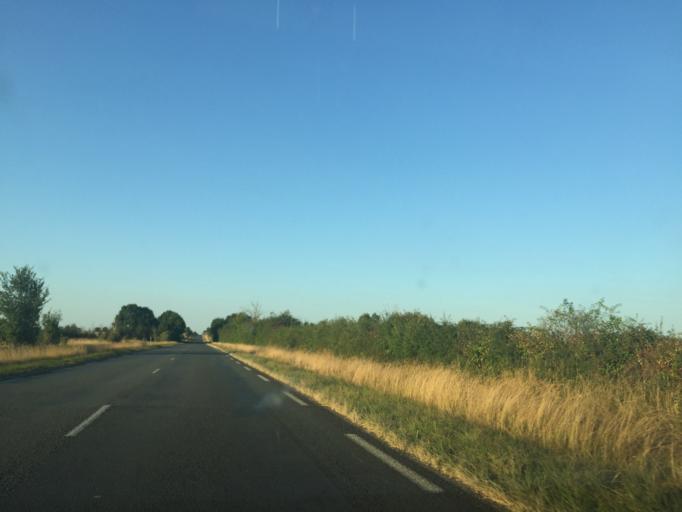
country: FR
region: Poitou-Charentes
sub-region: Departement de la Vienne
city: Saint-Sauvant
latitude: 46.3605
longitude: 0.0179
